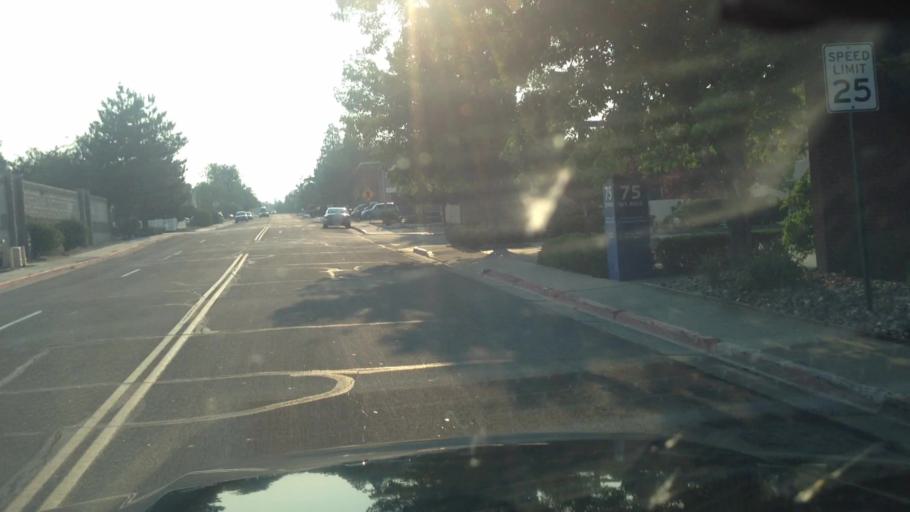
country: US
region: Nevada
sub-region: Washoe County
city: Reno
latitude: 39.5097
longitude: -119.8063
